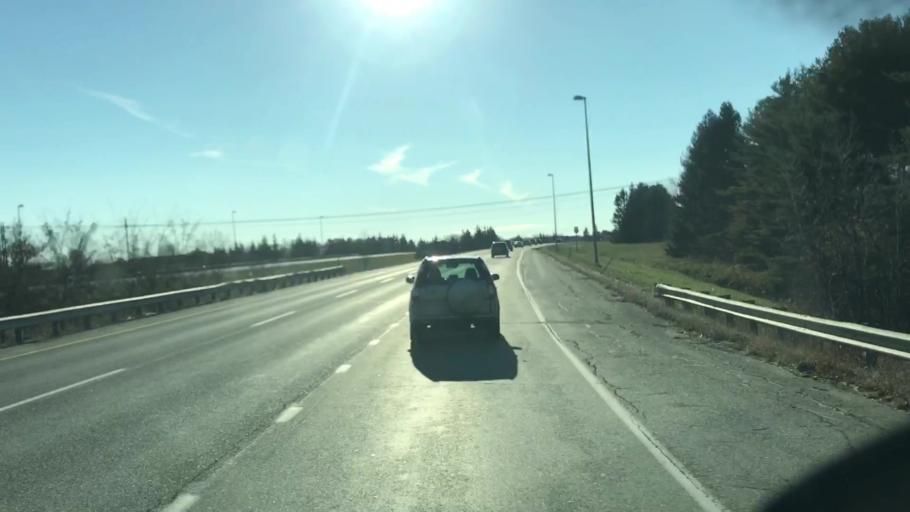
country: US
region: Maine
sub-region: Penobscot County
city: Brewer
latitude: 44.8308
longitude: -68.7437
